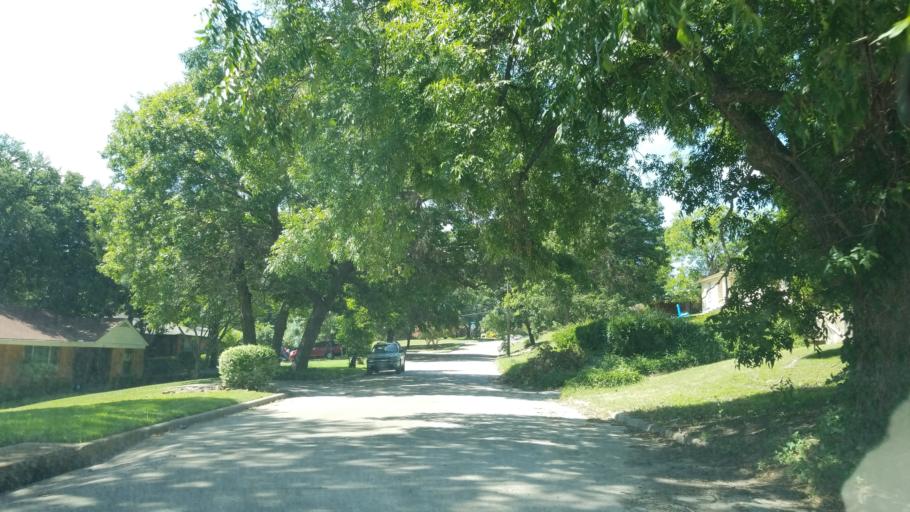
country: US
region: Texas
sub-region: Dallas County
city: Dallas
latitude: 32.7301
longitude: -96.7940
